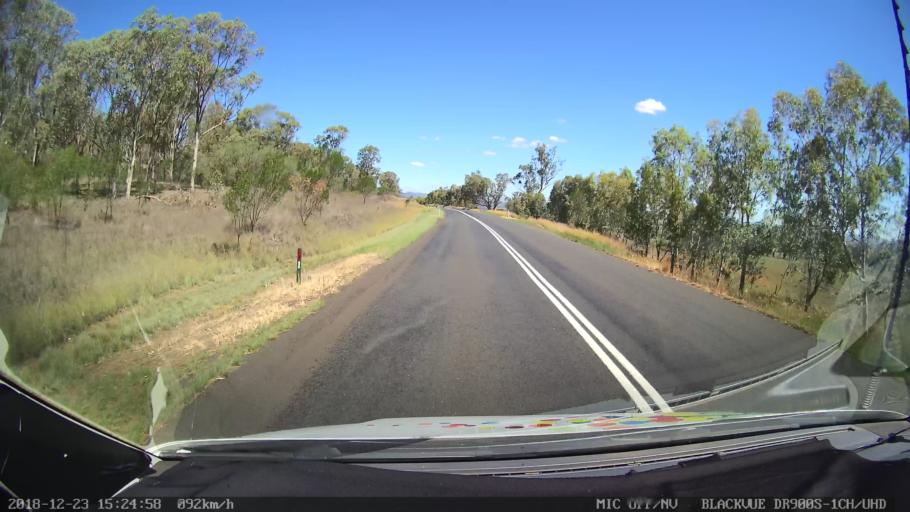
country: AU
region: New South Wales
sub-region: Tamworth Municipality
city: Manilla
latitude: -30.8986
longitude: 150.8262
